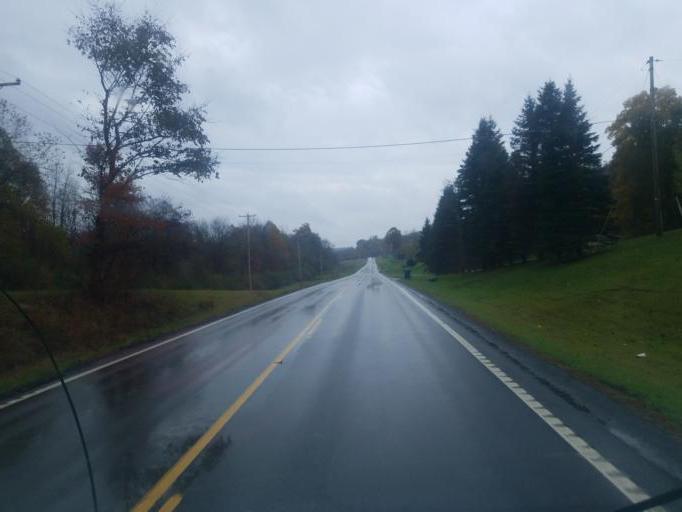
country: US
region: Ohio
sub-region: Muskingum County
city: Frazeysburg
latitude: 40.0707
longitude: -82.1589
